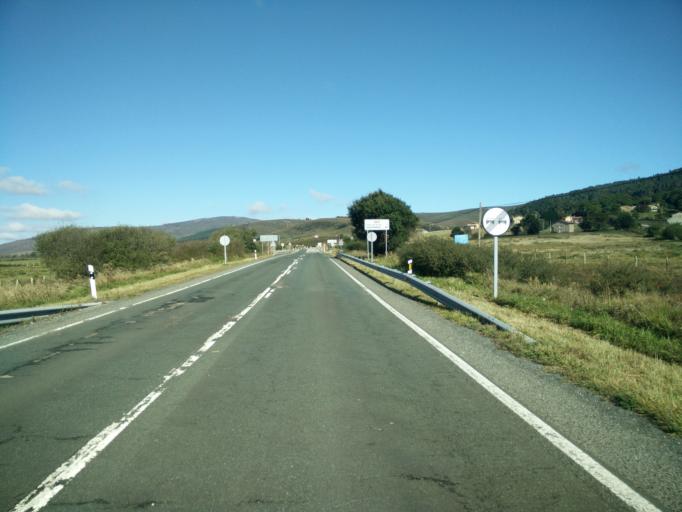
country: ES
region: Castille and Leon
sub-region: Provincia de Burgos
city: Arija
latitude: 43.0236
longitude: -3.8578
